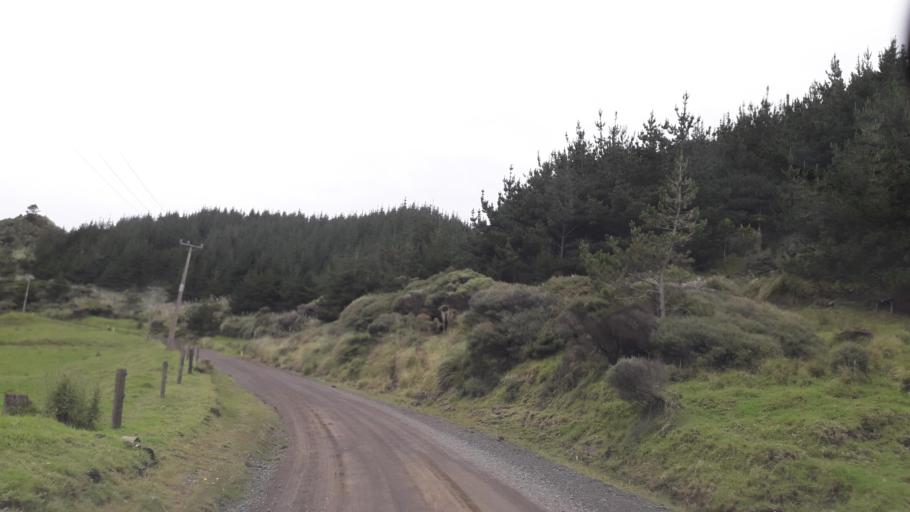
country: NZ
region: Northland
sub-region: Far North District
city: Ahipara
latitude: -35.4412
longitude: 173.2979
